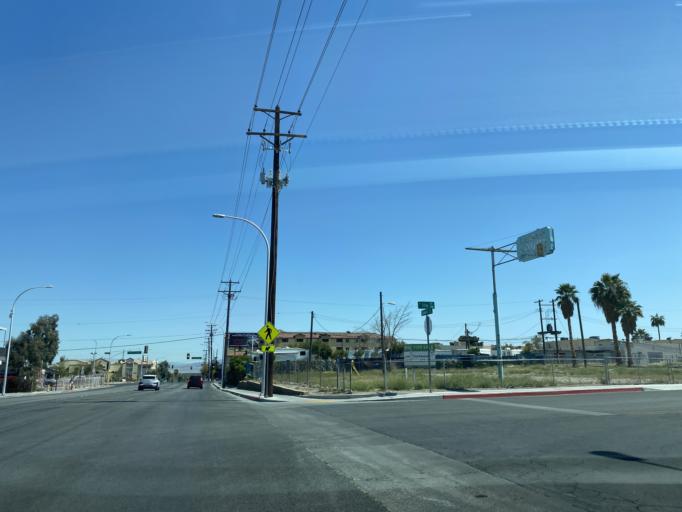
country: US
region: Nevada
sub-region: Clark County
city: Las Vegas
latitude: 36.1686
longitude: -115.1324
